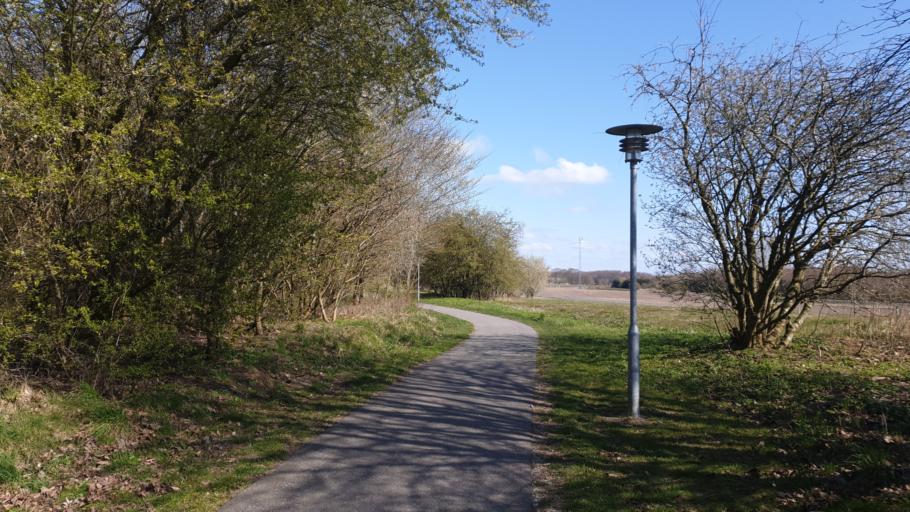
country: DK
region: Central Jutland
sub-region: Hedensted Kommune
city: Hedensted
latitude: 55.8086
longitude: 9.7038
